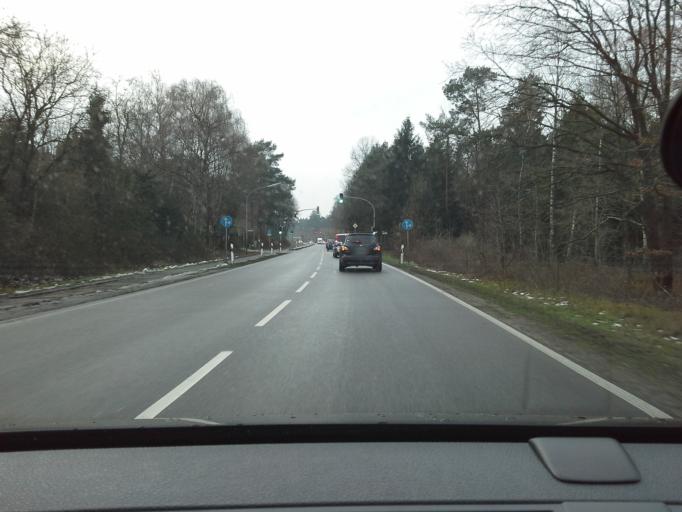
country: DE
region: Schleswig-Holstein
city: Henstedt-Ulzburg
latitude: 53.7483
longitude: 9.9975
